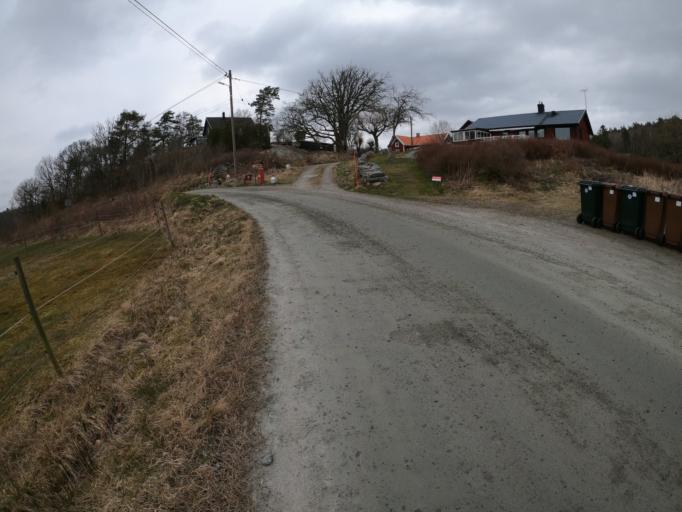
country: SE
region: Vaestra Goetaland
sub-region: Harryda Kommun
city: Molnlycke
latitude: 57.6292
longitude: 12.1078
